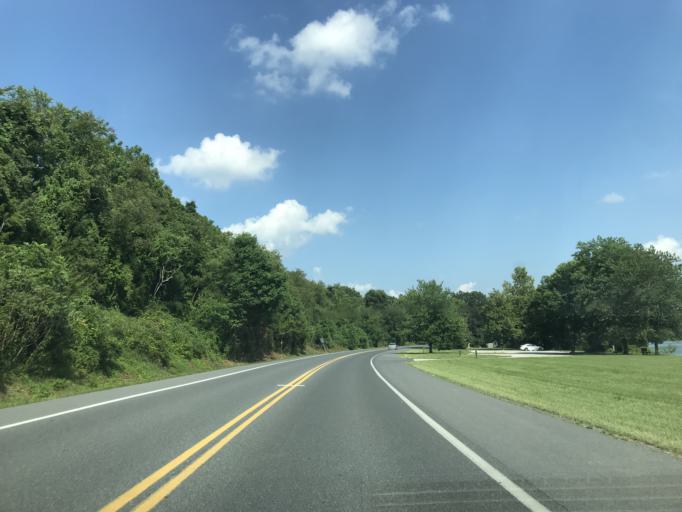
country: US
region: Pennsylvania
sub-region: York County
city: Parkville
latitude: 39.7916
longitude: -76.9234
